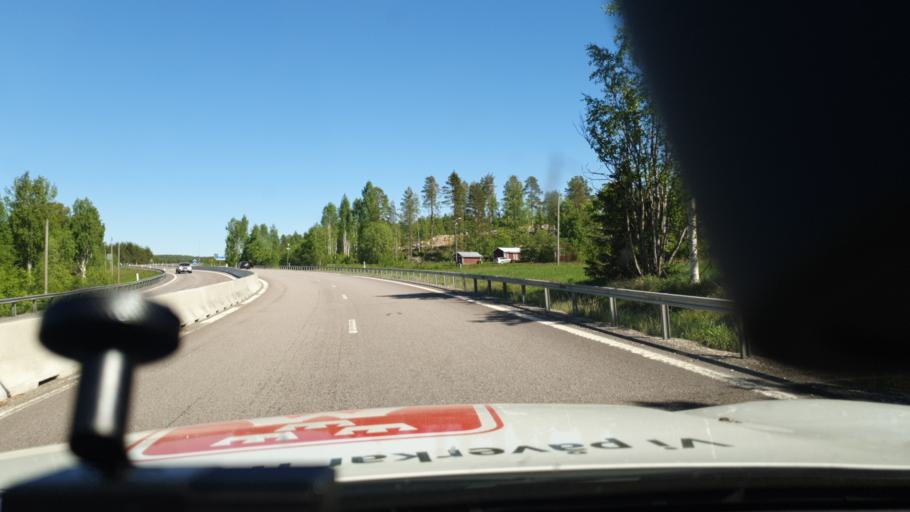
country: SE
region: Norrbotten
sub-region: Kalix Kommun
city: Rolfs
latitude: 65.8805
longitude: 22.9535
